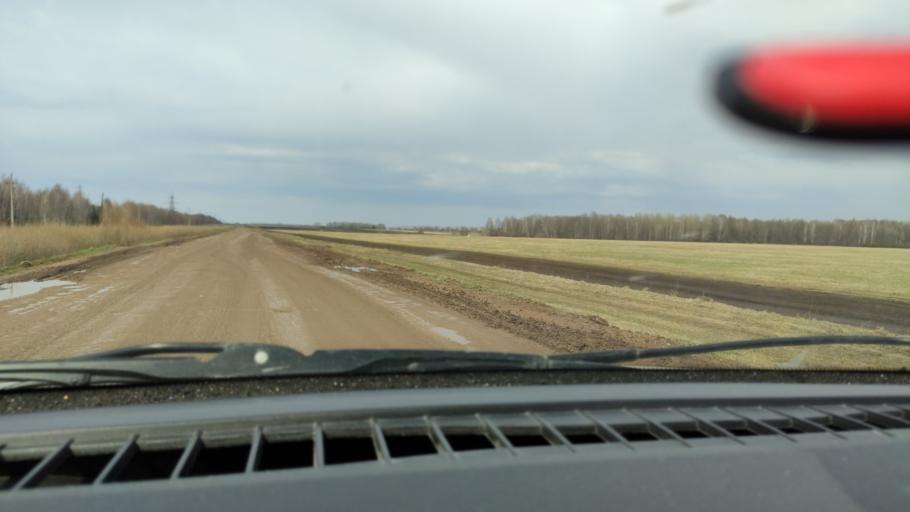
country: RU
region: Bashkortostan
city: Burayevo
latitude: 55.6551
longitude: 55.1733
